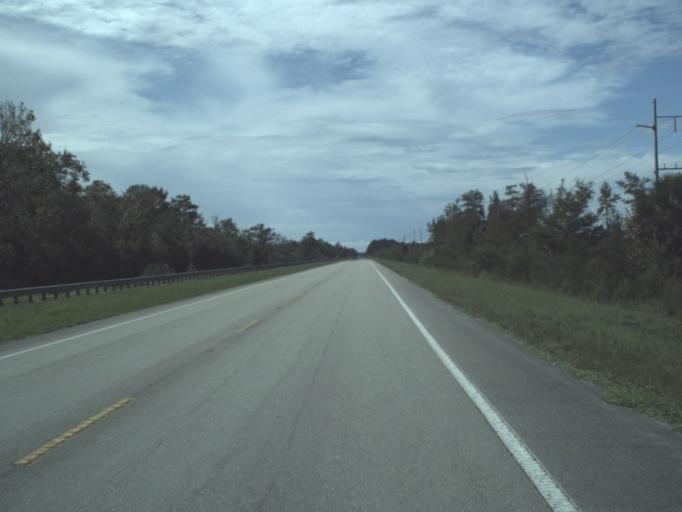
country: US
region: Florida
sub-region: Collier County
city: Lely Resort
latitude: 26.0179
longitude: -81.3458
